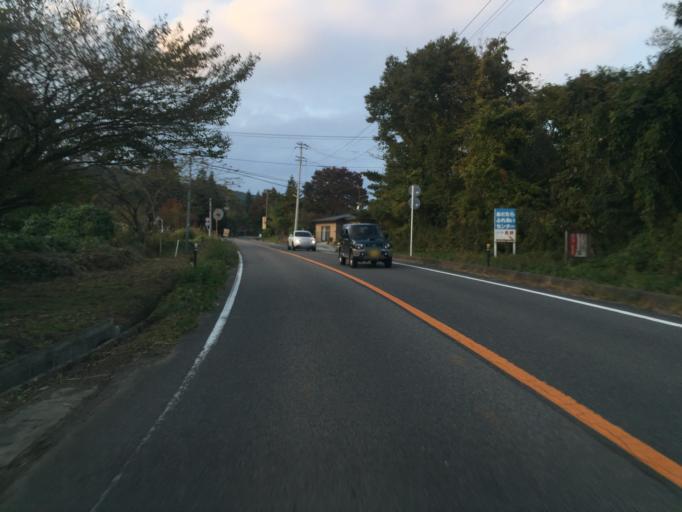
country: JP
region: Fukushima
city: Nihommatsu
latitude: 37.5974
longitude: 140.3564
